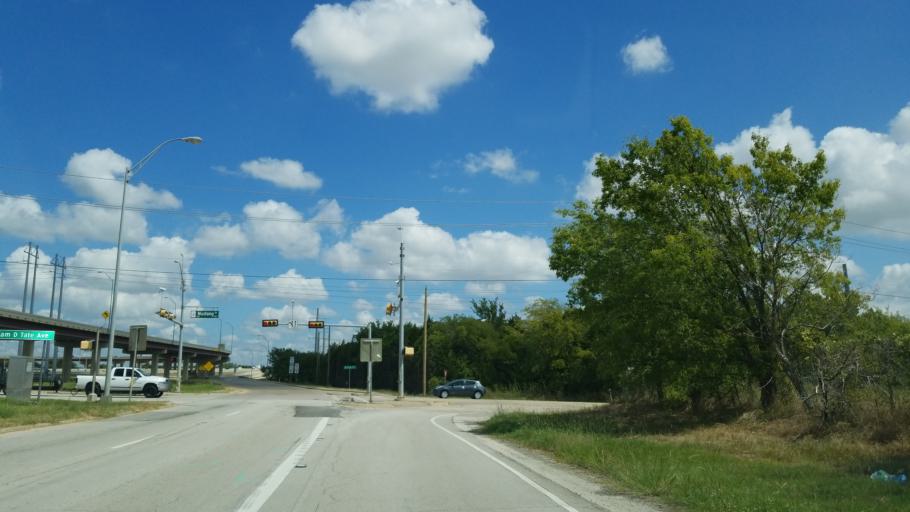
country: US
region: Texas
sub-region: Tarrant County
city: Grapevine
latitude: 32.9191
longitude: -97.0894
